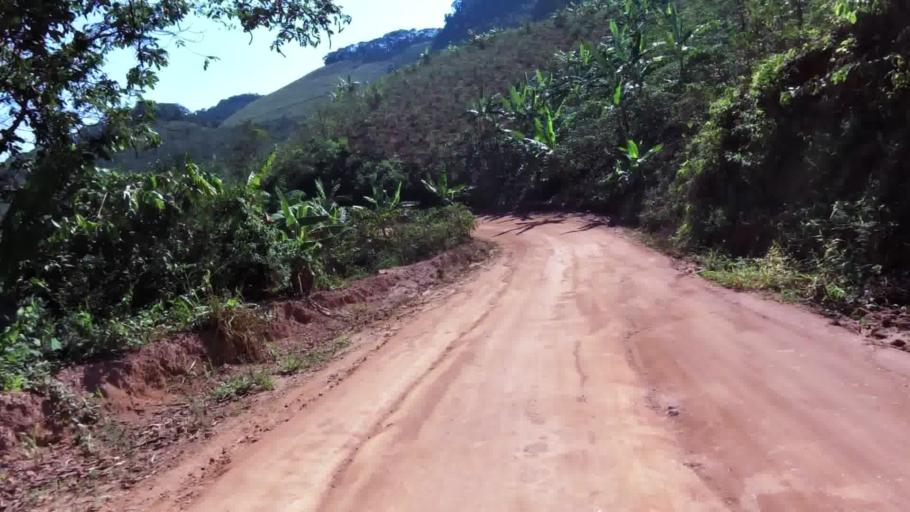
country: BR
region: Espirito Santo
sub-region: Alfredo Chaves
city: Alfredo Chaves
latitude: -20.5696
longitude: -40.7827
